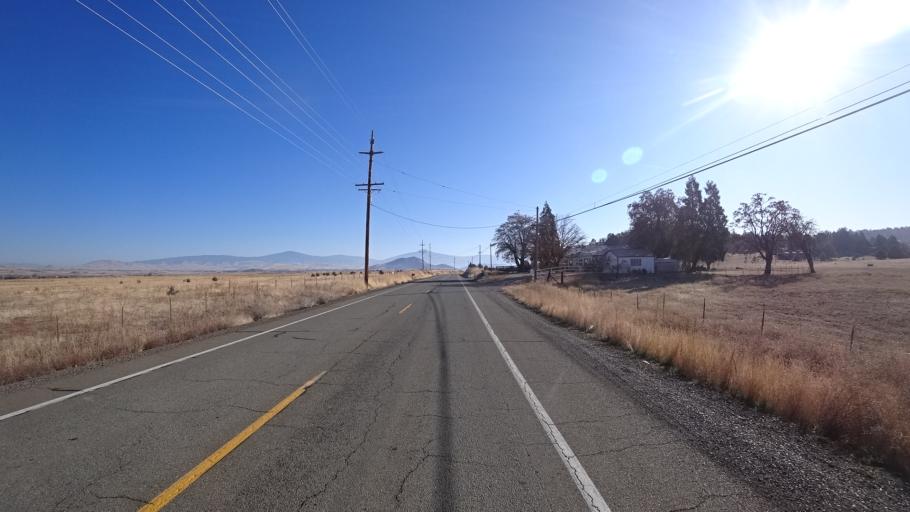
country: US
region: California
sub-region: Siskiyou County
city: Yreka
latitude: 41.7110
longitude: -122.5852
